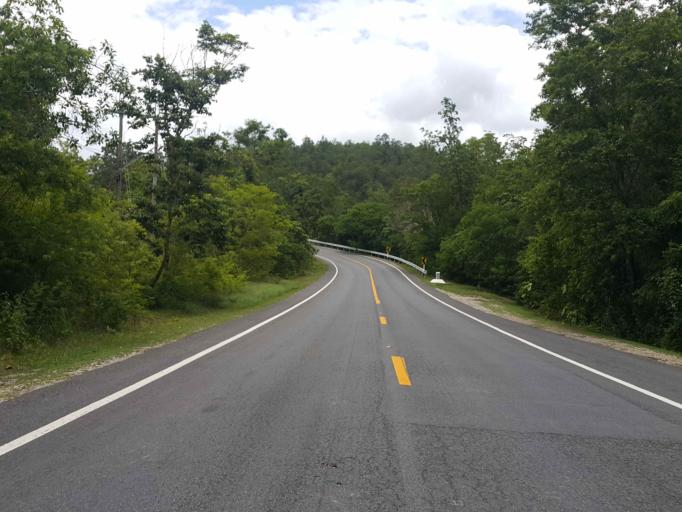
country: TH
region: Chiang Mai
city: Chom Thong
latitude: 18.5183
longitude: 98.6563
